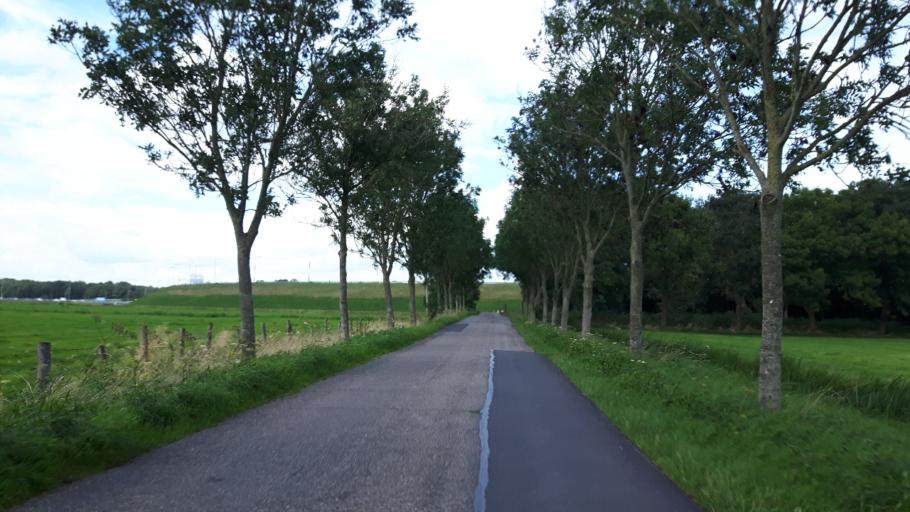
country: NL
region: Utrecht
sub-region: Gemeente Nieuwegein
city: Nieuwegein
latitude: 52.0610
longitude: 5.0658
